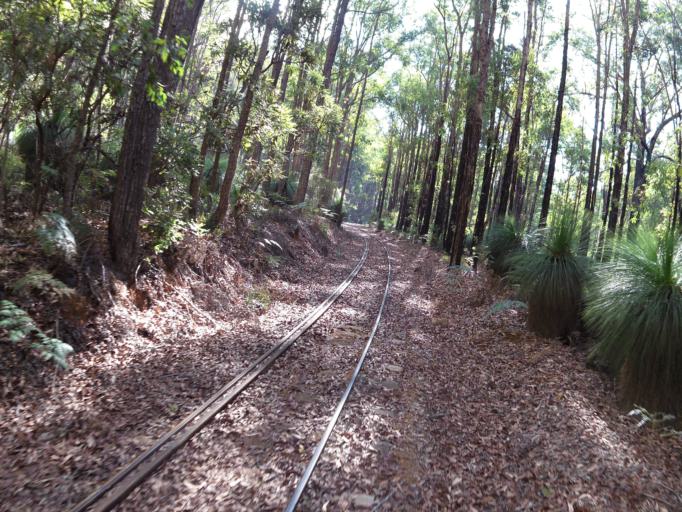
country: AU
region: Western Australia
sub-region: Waroona
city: Waroona
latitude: -32.7303
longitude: 116.1134
